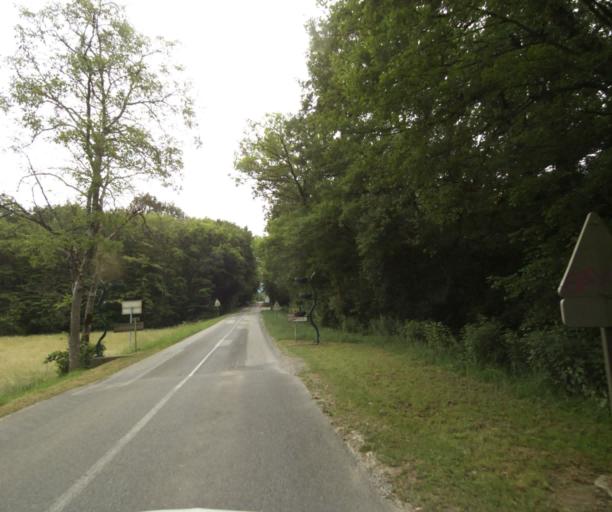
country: FR
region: Rhone-Alpes
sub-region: Departement de la Haute-Savoie
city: Sciez
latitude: 46.3245
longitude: 6.3939
